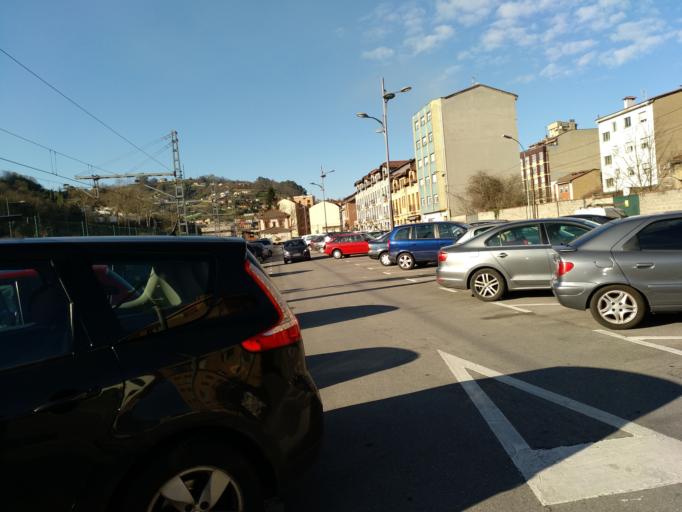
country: ES
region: Asturias
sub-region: Province of Asturias
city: Sama
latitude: 43.2912
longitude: -5.6776
